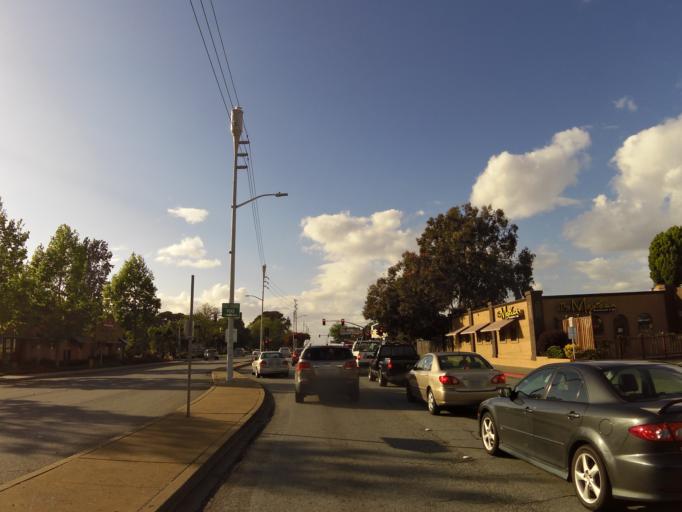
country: US
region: California
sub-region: Alameda County
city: San Lorenzo
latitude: 37.6671
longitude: -122.1189
